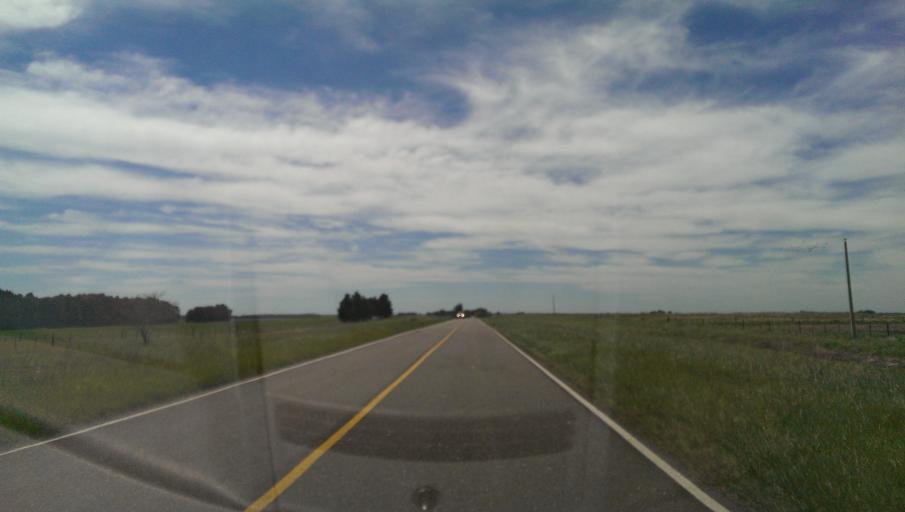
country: AR
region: Buenos Aires
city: Coronel Pringles
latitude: -37.7595
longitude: -61.6653
